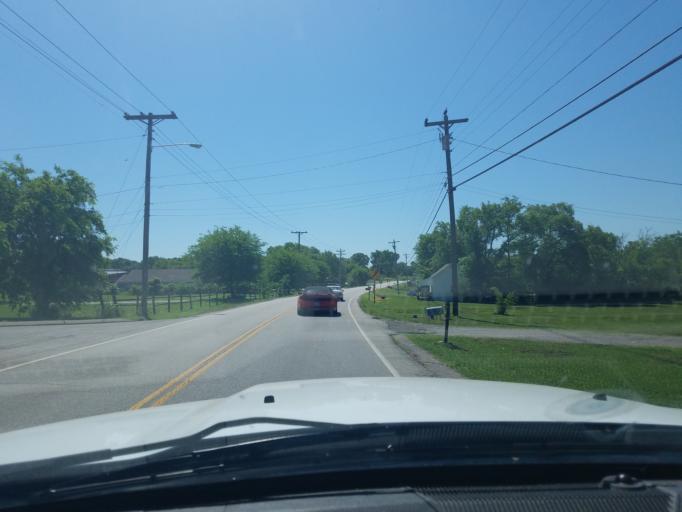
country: US
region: Tennessee
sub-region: Wilson County
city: Lebanon
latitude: 36.1931
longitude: -86.2837
